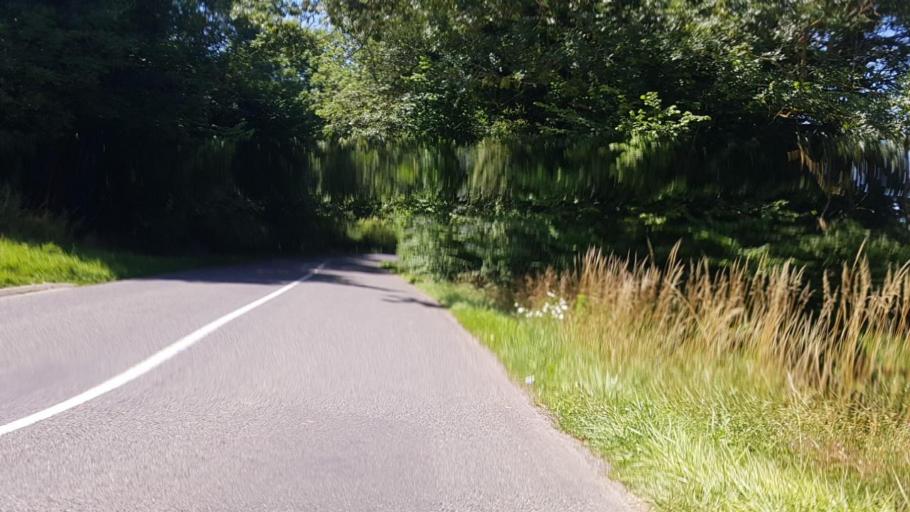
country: FR
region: Ile-de-France
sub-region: Departement de Seine-et-Marne
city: Moussy-le-Vieux
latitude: 49.0280
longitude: 2.6404
